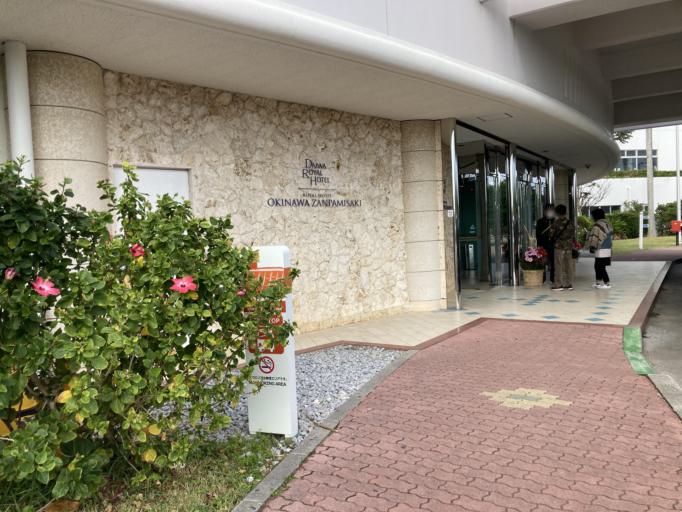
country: JP
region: Okinawa
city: Ishikawa
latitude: 26.4348
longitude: 127.7186
